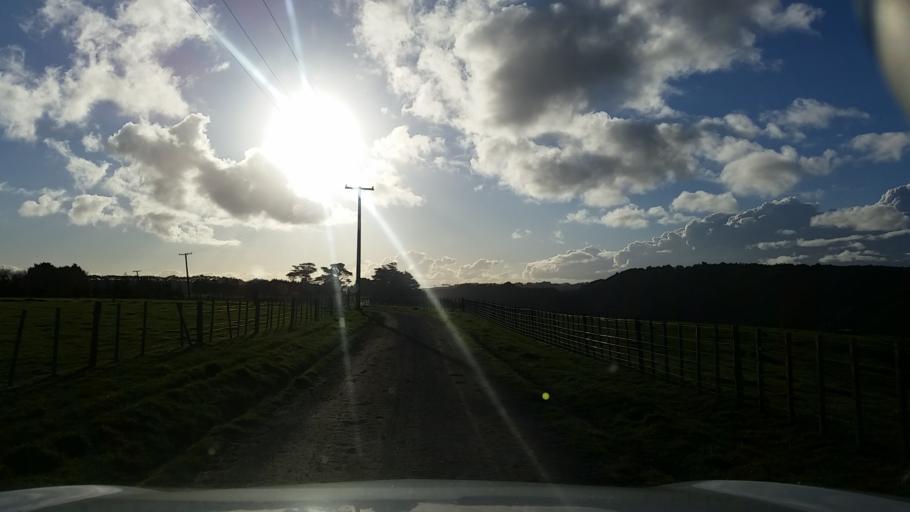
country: NZ
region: Taranaki
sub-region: South Taranaki District
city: Patea
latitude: -39.6175
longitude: 174.4977
